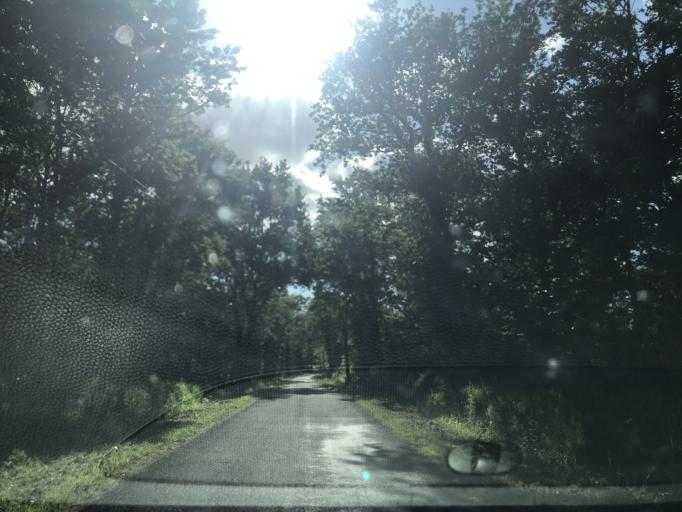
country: FR
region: Poitou-Charentes
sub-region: Departement de la Charente
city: Chalais
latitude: 45.2756
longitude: -0.0319
